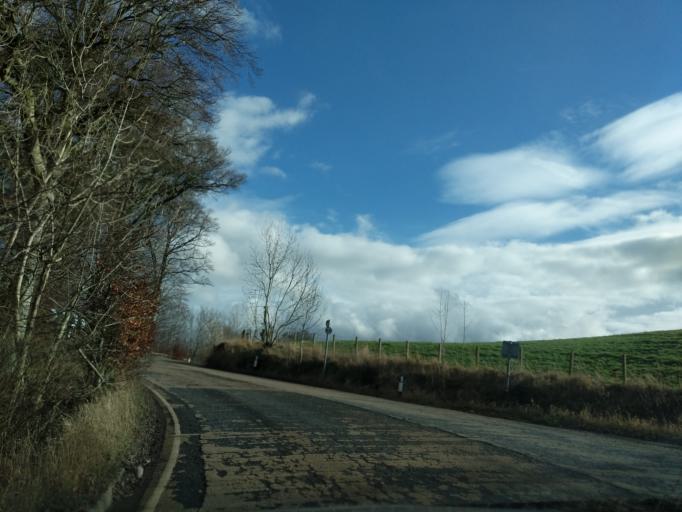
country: GB
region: Scotland
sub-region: South Lanarkshire
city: Lanark
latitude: 55.6752
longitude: -3.8297
